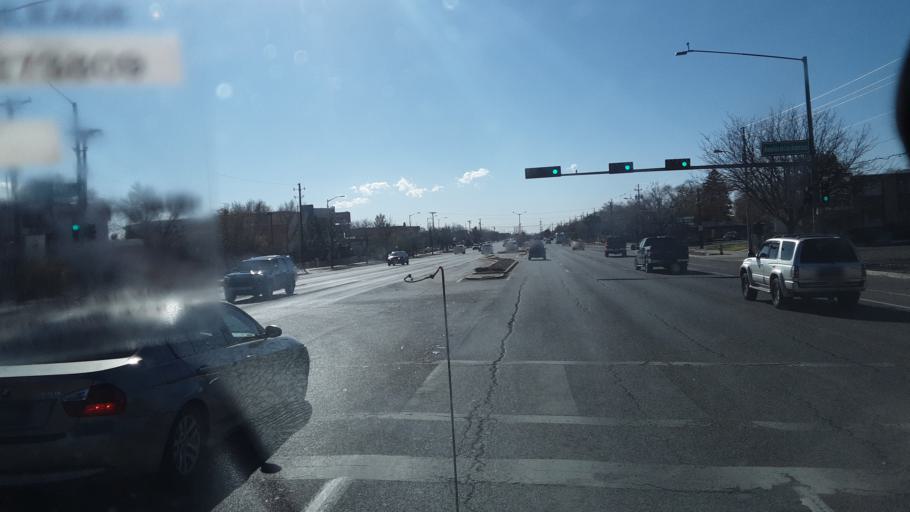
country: US
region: New Mexico
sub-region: Santa Fe County
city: Agua Fria
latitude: 35.6485
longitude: -106.0028
